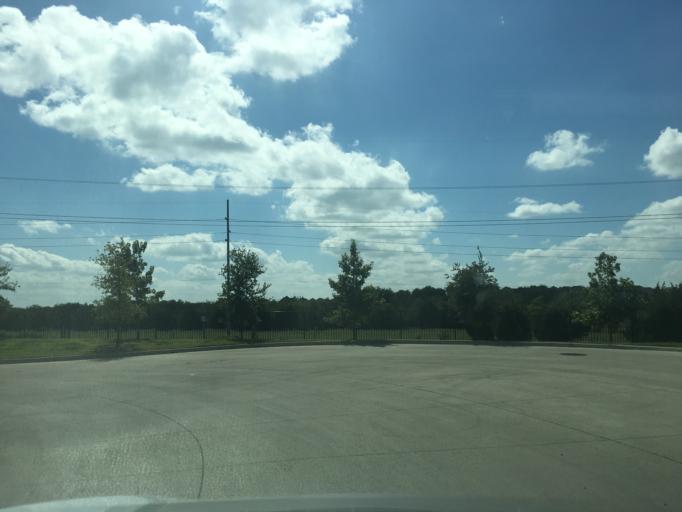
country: US
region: Texas
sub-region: Dallas County
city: Sachse
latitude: 32.9682
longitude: -96.5739
